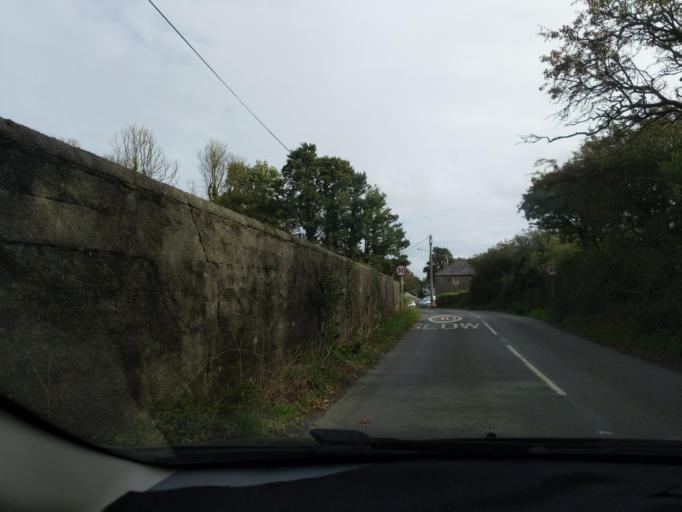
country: GB
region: England
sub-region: Cornwall
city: Mevagissey
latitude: 50.2473
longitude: -4.8102
